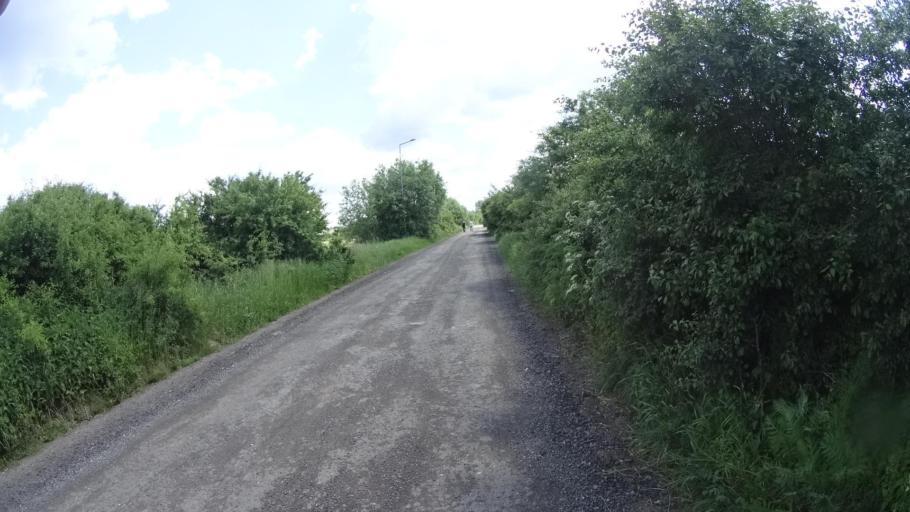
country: PL
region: Masovian Voivodeship
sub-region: Powiat pruszkowski
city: Nadarzyn
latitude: 52.0569
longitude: 20.8238
